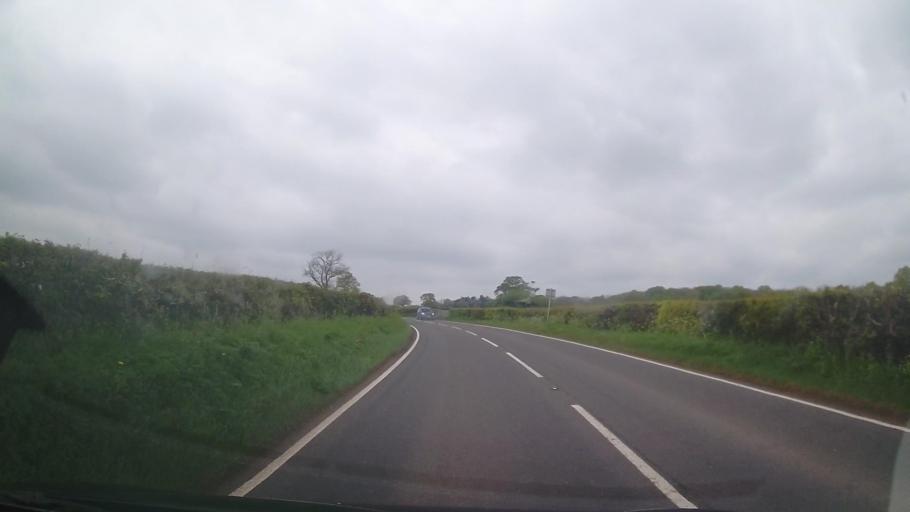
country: GB
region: Wales
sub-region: Wrexham
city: Overton
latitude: 52.9825
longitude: -2.9751
